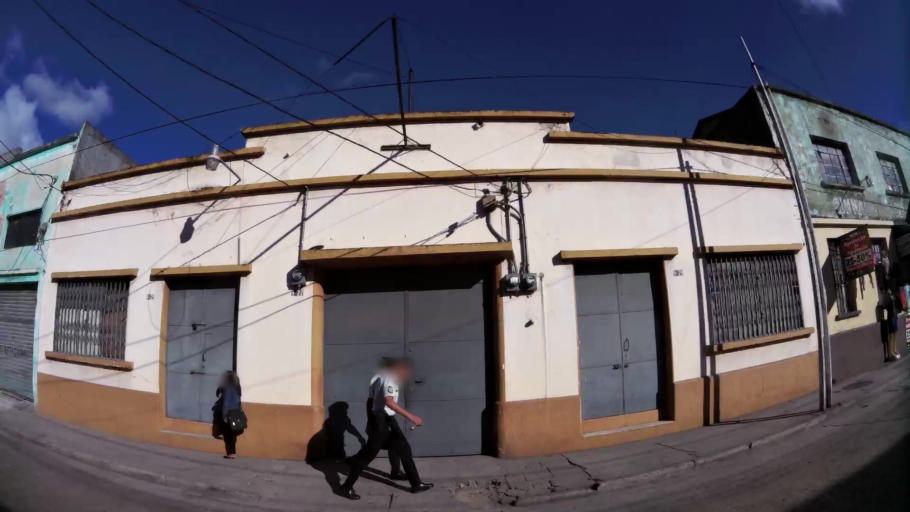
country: GT
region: Guatemala
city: Guatemala City
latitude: 14.6387
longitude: -90.5060
